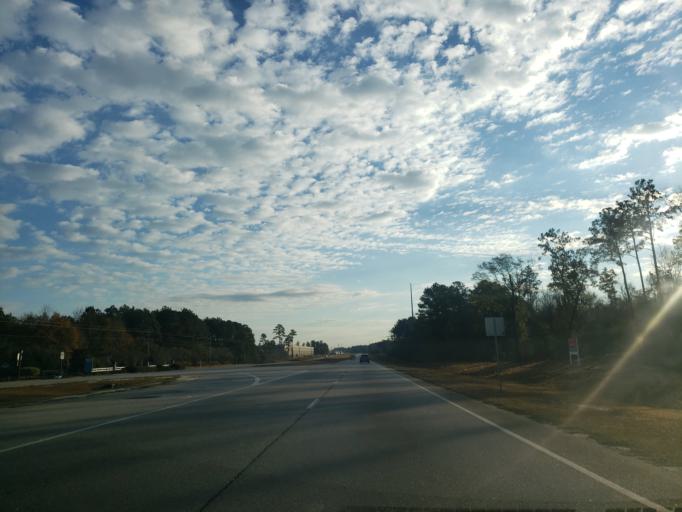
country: US
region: Georgia
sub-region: Chatham County
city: Pooler
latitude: 32.1623
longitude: -81.2558
